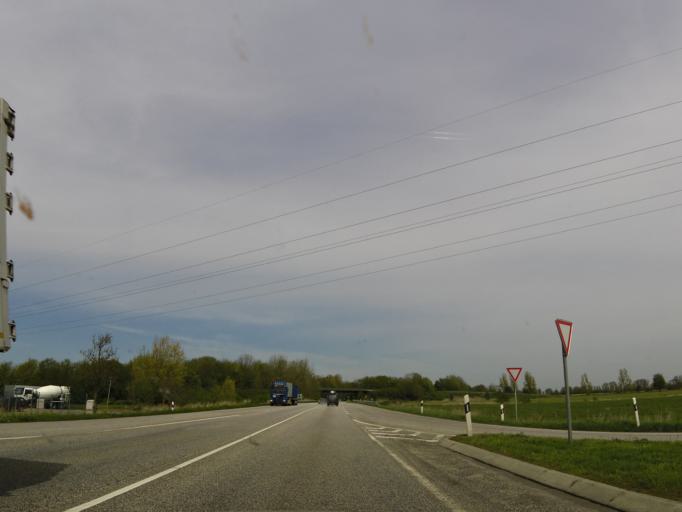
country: DE
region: Schleswig-Holstein
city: Tonning
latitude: 54.3269
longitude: 8.9543
